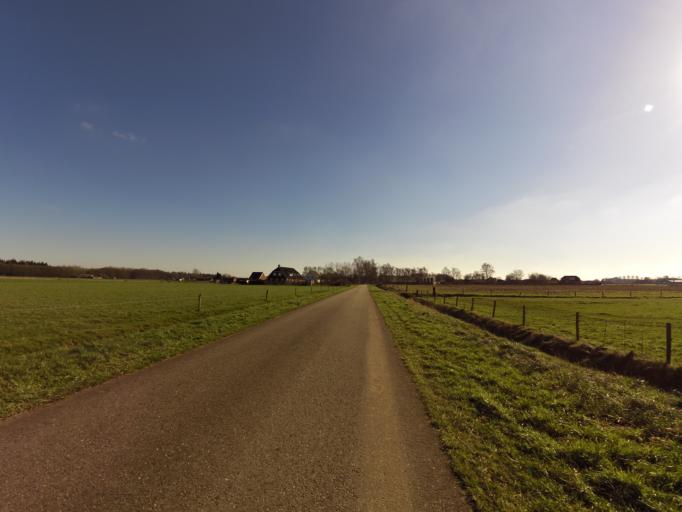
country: NL
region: Gelderland
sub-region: Gemeente Doesburg
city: Doesburg
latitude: 51.9506
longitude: 6.1672
